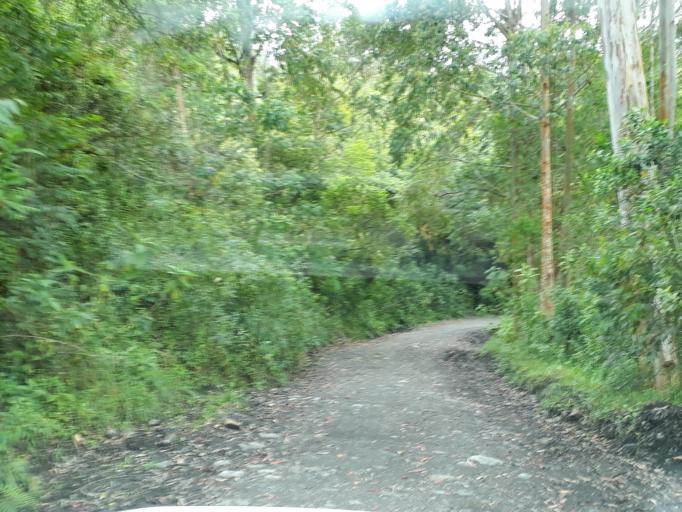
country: CO
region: Cundinamarca
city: Junin
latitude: 4.7823
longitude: -73.6897
